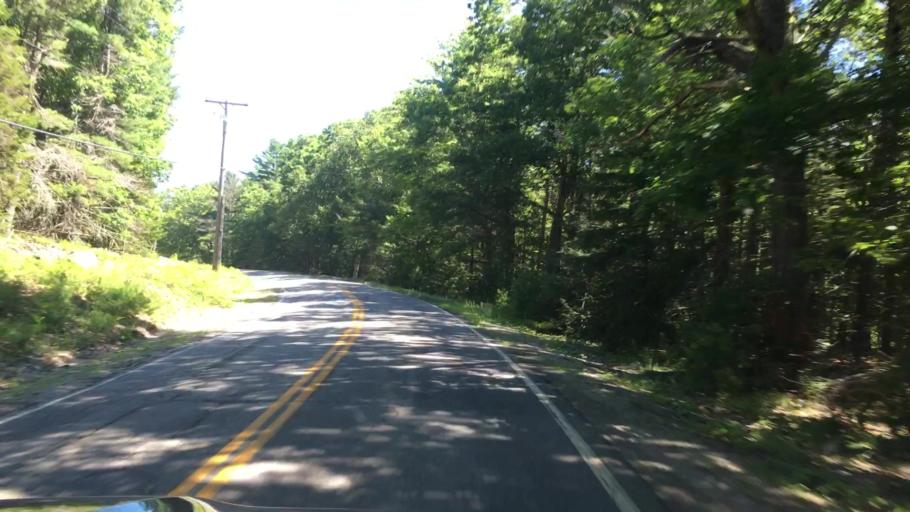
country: US
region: Maine
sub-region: Hancock County
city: Penobscot
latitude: 44.4776
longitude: -68.6916
